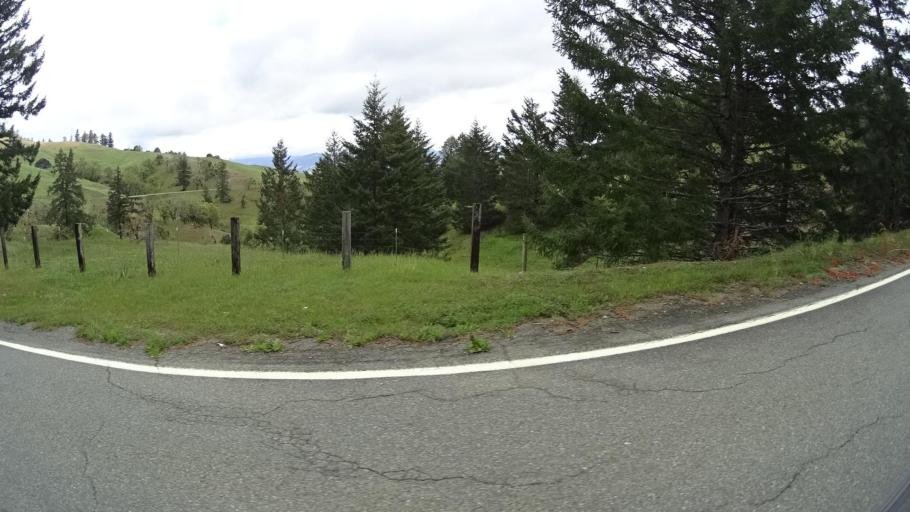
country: US
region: California
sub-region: Humboldt County
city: Redway
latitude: 40.1020
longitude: -123.6844
